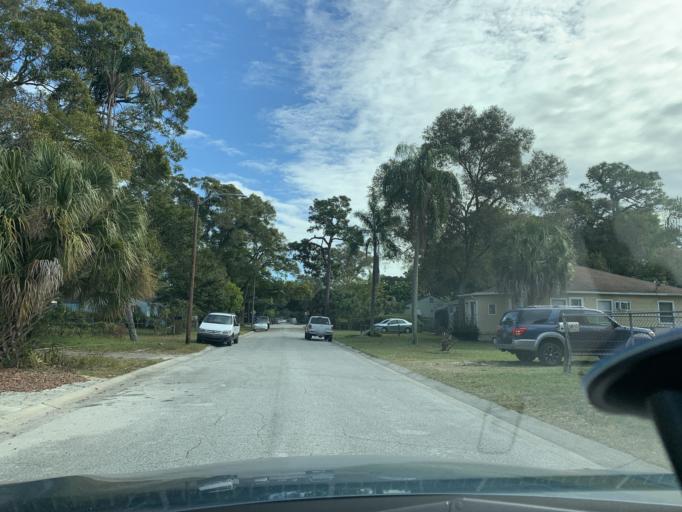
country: US
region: Florida
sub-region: Pinellas County
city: Lealman
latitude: 27.7966
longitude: -82.6609
